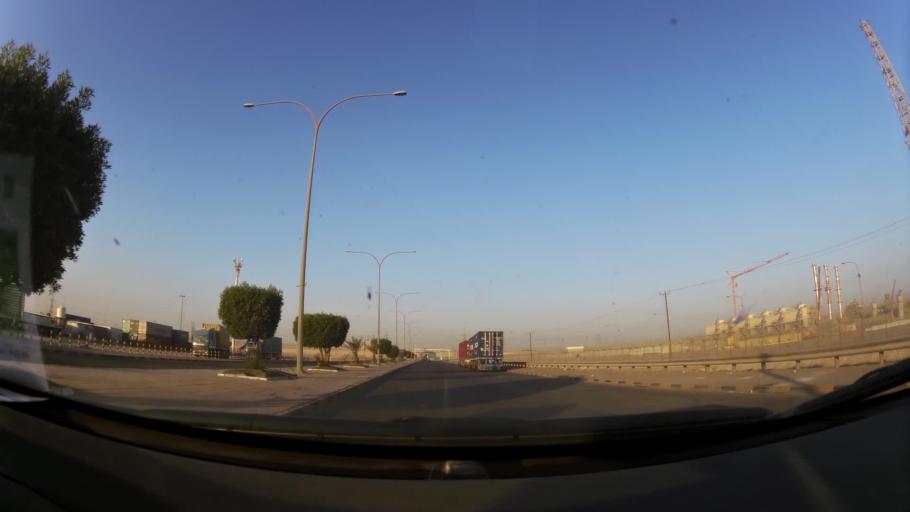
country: KW
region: Al Ahmadi
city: Al Fahahil
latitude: 29.0457
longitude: 48.1196
